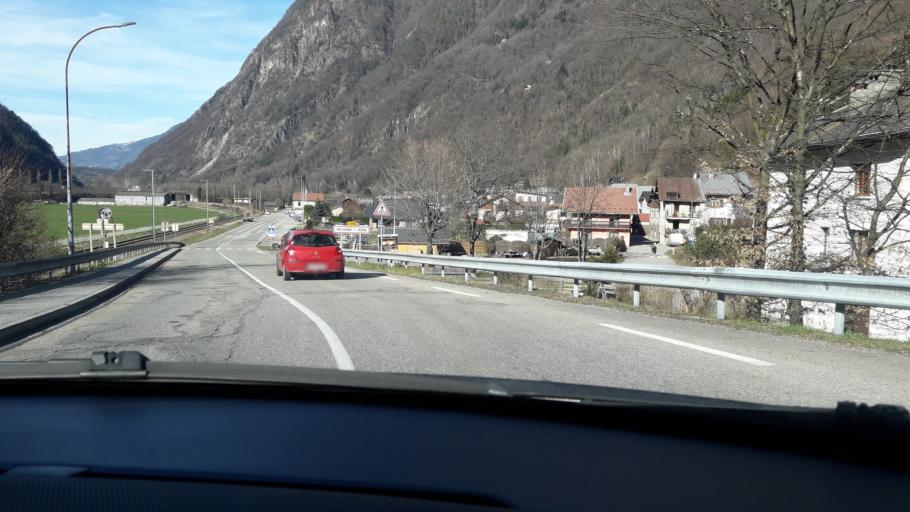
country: FR
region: Rhone-Alpes
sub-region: Departement de la Savoie
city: Aigueblanche
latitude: 45.5553
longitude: 6.4691
